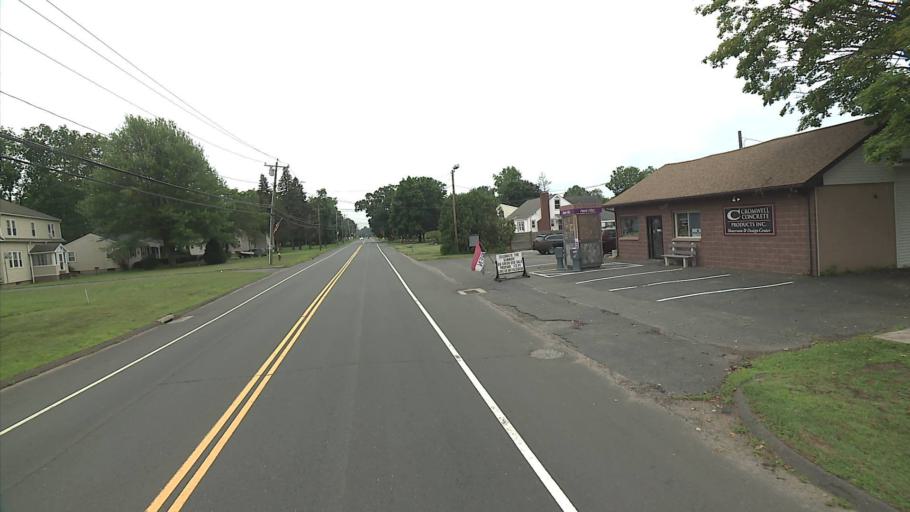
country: US
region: Connecticut
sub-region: Middlesex County
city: Cromwell
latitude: 41.6319
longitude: -72.6500
